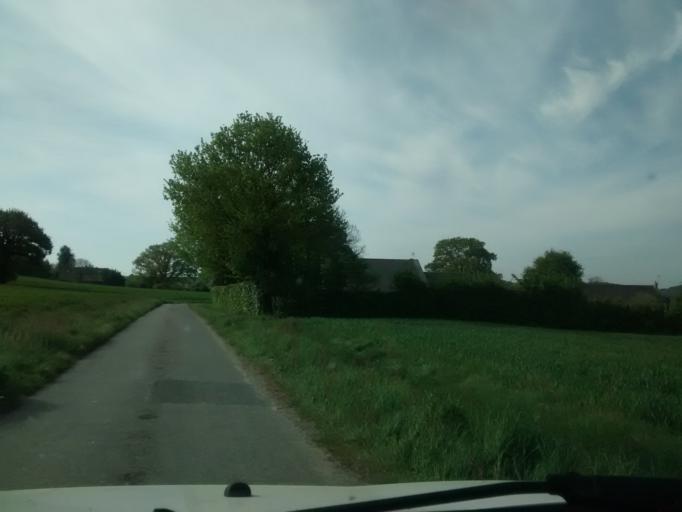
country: FR
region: Brittany
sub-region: Departement d'Ille-et-Vilaine
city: Bain-de-Bretagne
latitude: 47.8050
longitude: -1.7109
